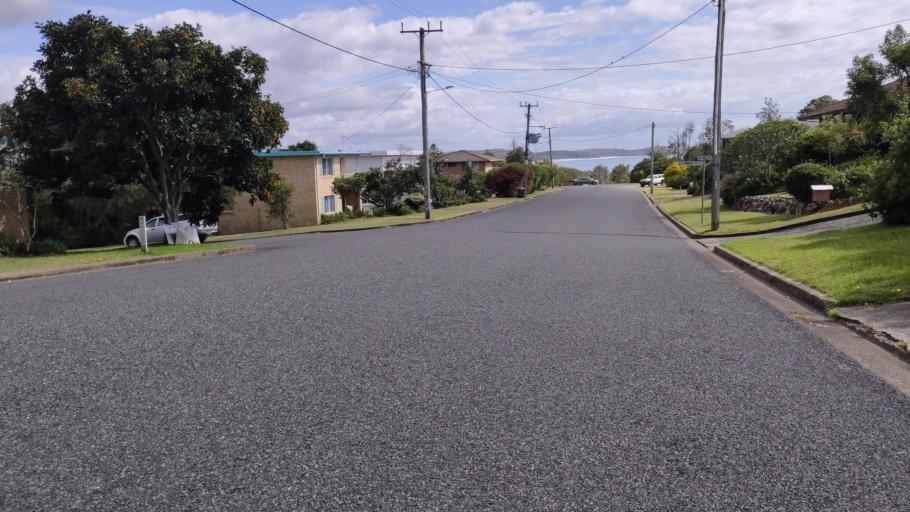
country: AU
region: New South Wales
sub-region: Port Macquarie-Hastings
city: North Haven
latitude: -31.6419
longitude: 152.8353
